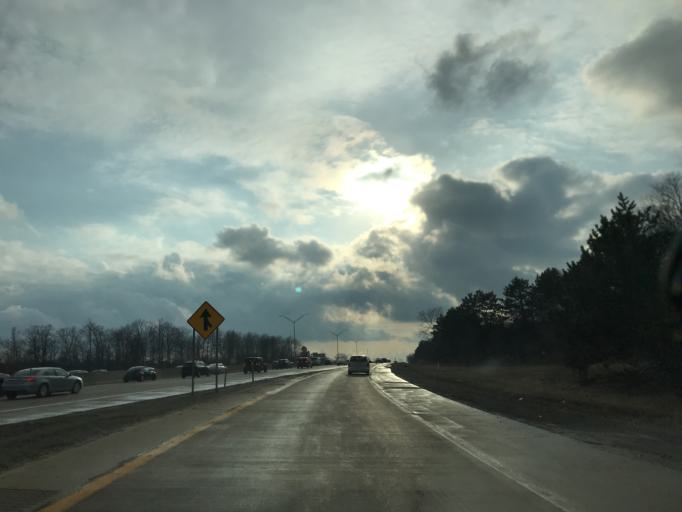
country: US
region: Michigan
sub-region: Oakland County
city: Farmington Hills
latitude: 42.4963
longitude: -83.3613
